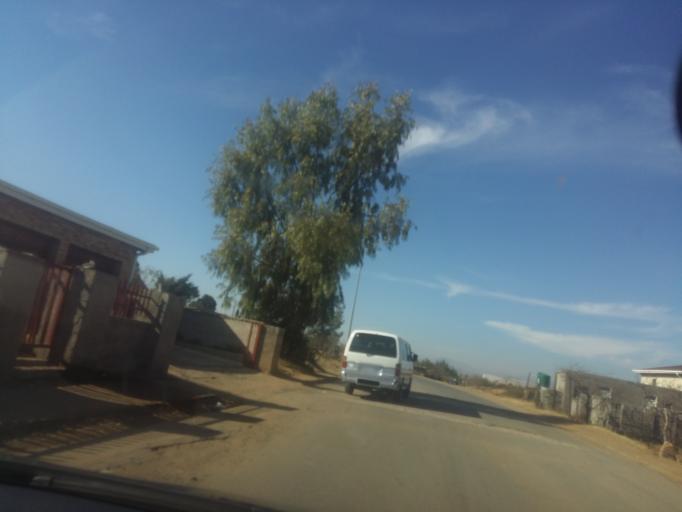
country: LS
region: Maseru
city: Maseru
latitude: -29.3927
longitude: 27.5226
